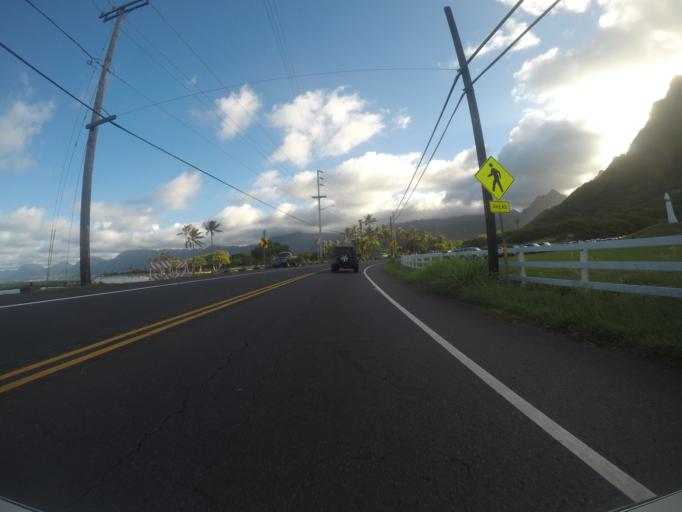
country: US
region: Hawaii
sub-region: Honolulu County
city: Ka'a'awa
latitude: 21.5179
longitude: -157.8362
